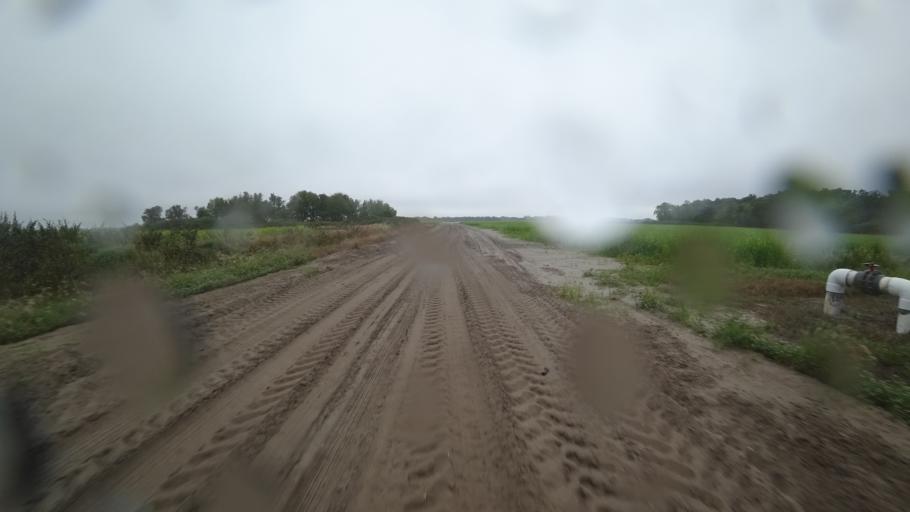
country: US
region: Florida
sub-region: Sarasota County
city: Warm Mineral Springs
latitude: 27.2900
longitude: -82.1641
